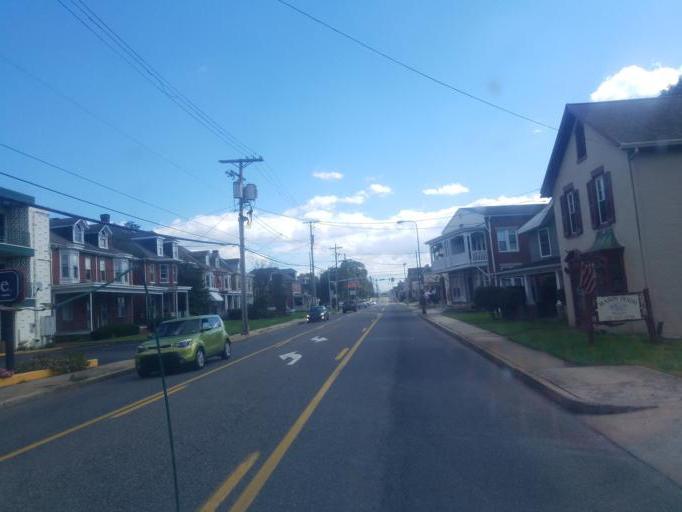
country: US
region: Pennsylvania
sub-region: Franklin County
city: Chambersburg
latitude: 39.9343
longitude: -77.6505
